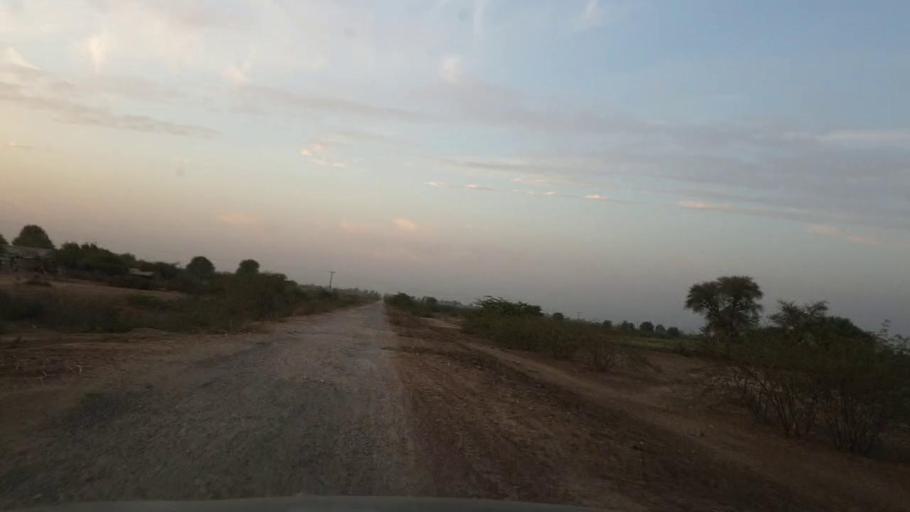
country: PK
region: Sindh
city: Kunri
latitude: 25.1331
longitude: 69.5644
